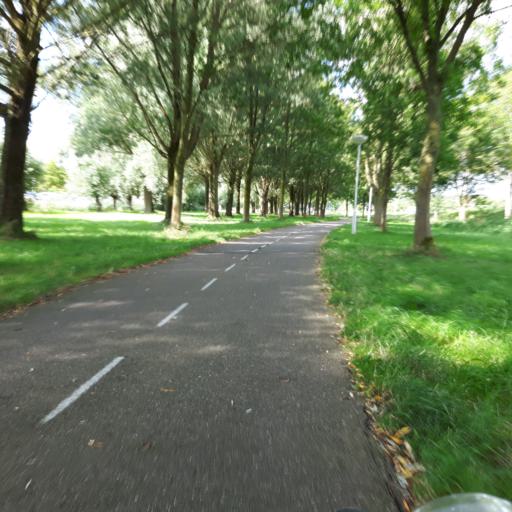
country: NL
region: Zeeland
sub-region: Gemeente Goes
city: Goes
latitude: 51.4925
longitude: 3.8685
